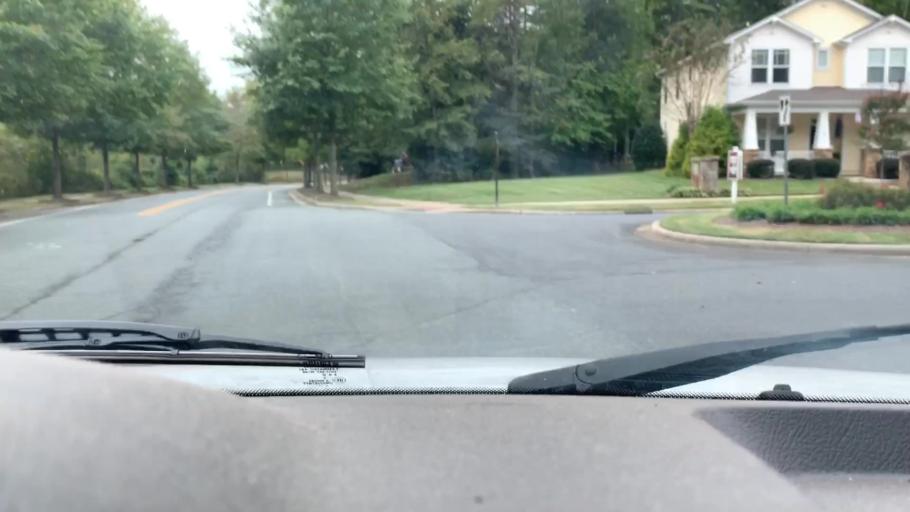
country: US
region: North Carolina
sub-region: Mecklenburg County
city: Huntersville
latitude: 35.4222
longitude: -80.8726
